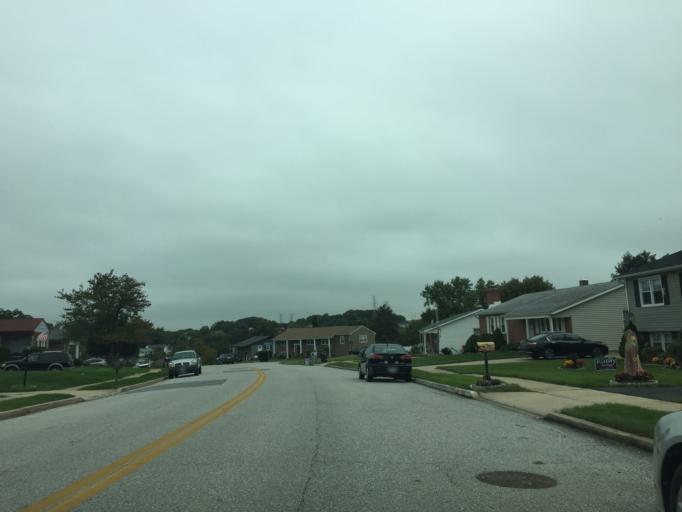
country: US
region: Maryland
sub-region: Baltimore County
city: Rossville
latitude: 39.3362
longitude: -76.4995
